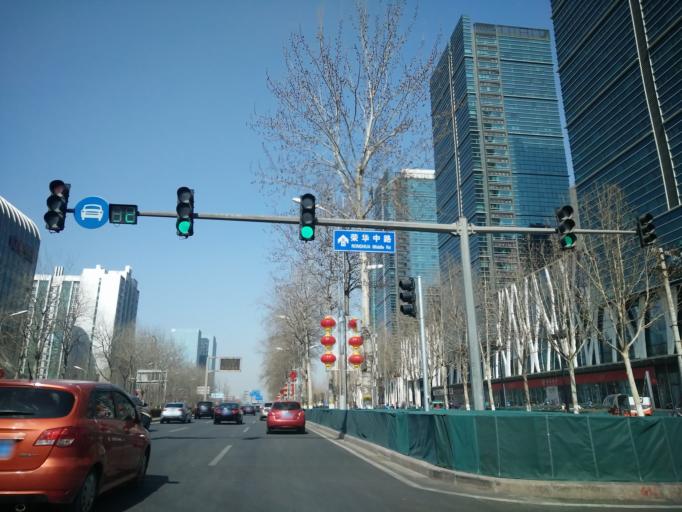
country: CN
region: Beijing
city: Jiugong
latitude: 39.8015
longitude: 116.4962
